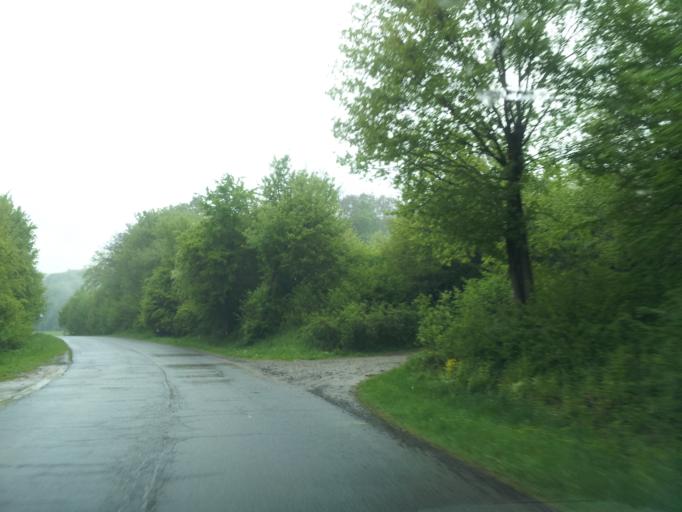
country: HU
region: Baranya
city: Komlo
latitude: 46.1999
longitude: 18.3035
